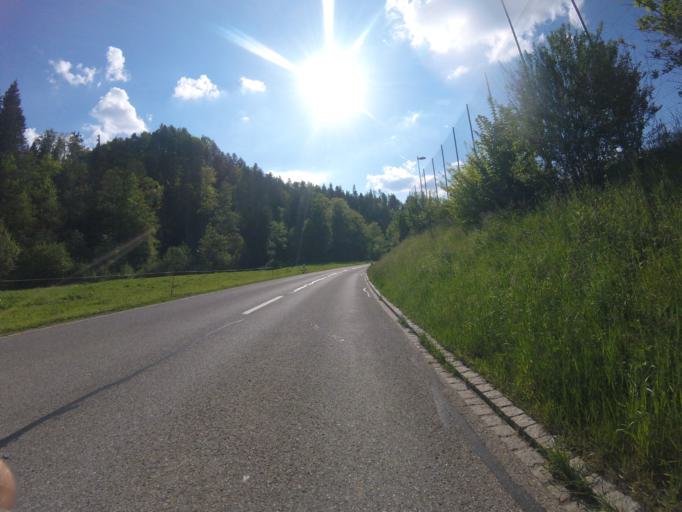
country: CH
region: Saint Gallen
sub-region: Wahlkreis Toggenburg
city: Mogelsberg
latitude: 47.3611
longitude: 9.1551
